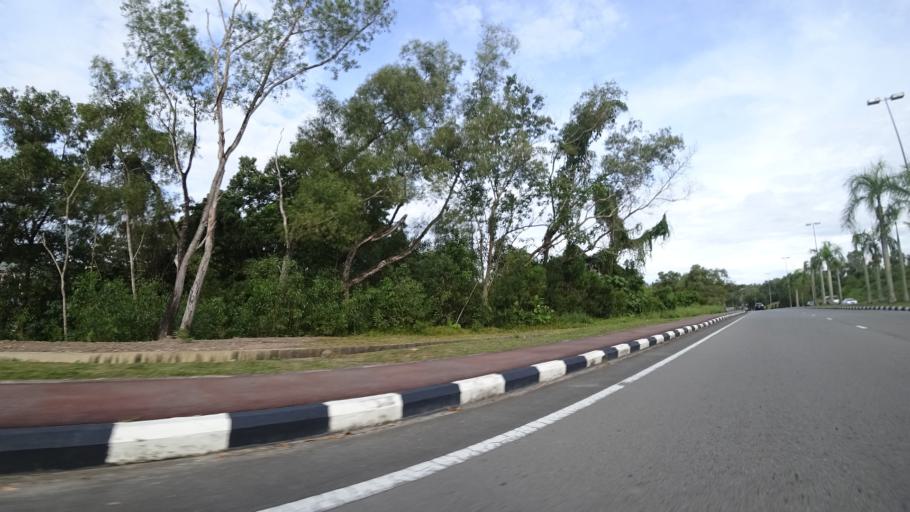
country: BN
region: Brunei and Muara
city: Bandar Seri Begawan
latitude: 4.9192
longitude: 114.9457
